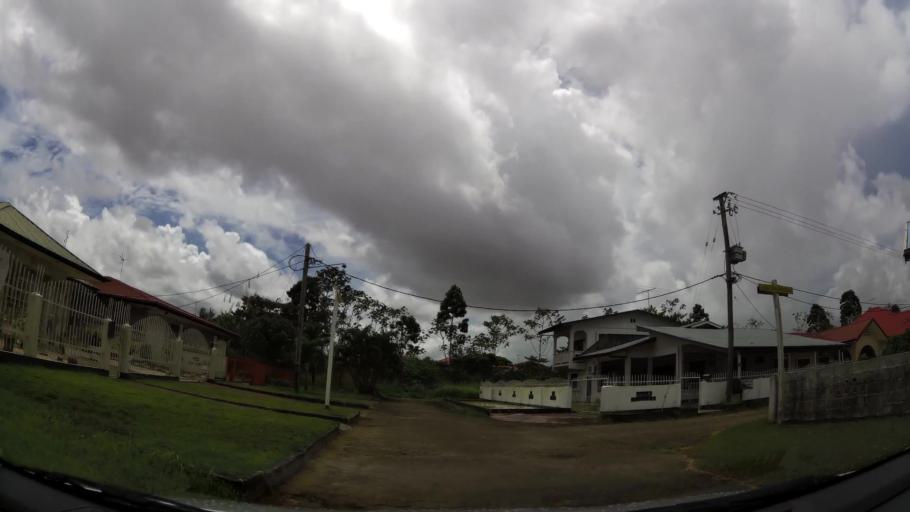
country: SR
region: Paramaribo
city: Paramaribo
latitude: 5.8269
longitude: -55.2225
